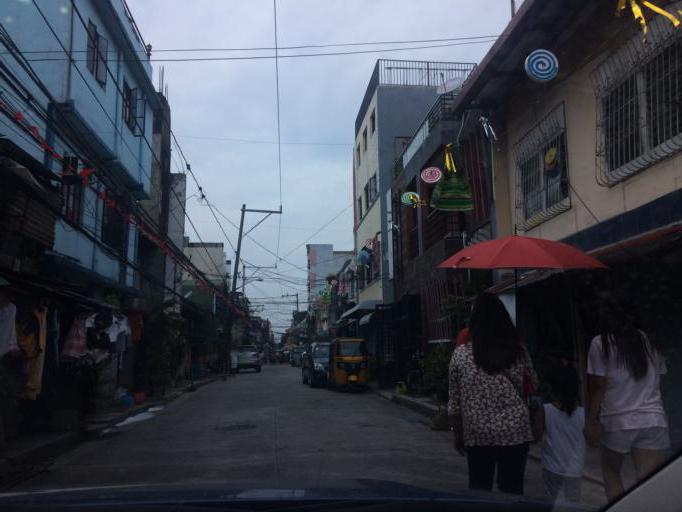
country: PH
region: Metro Manila
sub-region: Makati City
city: Makati City
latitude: 14.5403
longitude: 121.0030
